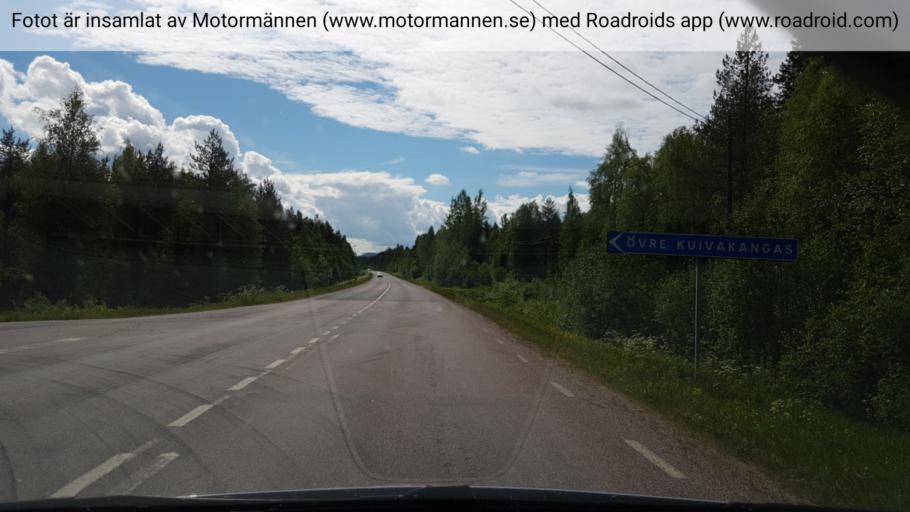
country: SE
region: Norrbotten
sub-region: Overtornea Kommun
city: OEvertornea
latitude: 66.4449
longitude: 23.6168
